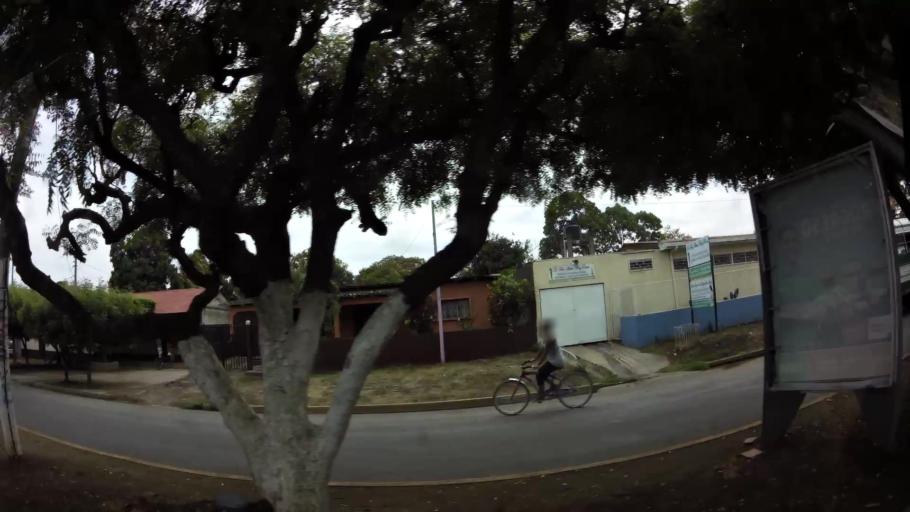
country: NI
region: Rivas
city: Rivas
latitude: 11.4434
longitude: -85.8275
